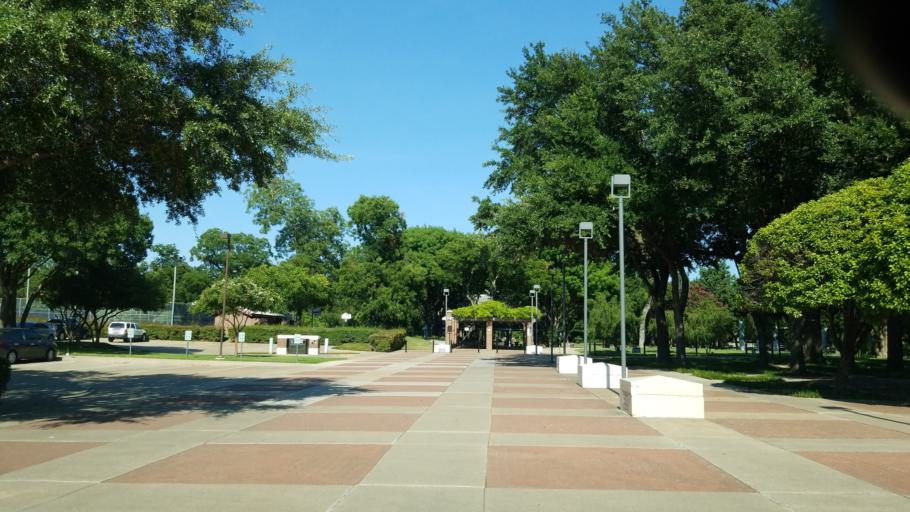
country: US
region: Texas
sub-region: Dallas County
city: Farmers Branch
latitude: 32.9214
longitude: -96.8933
